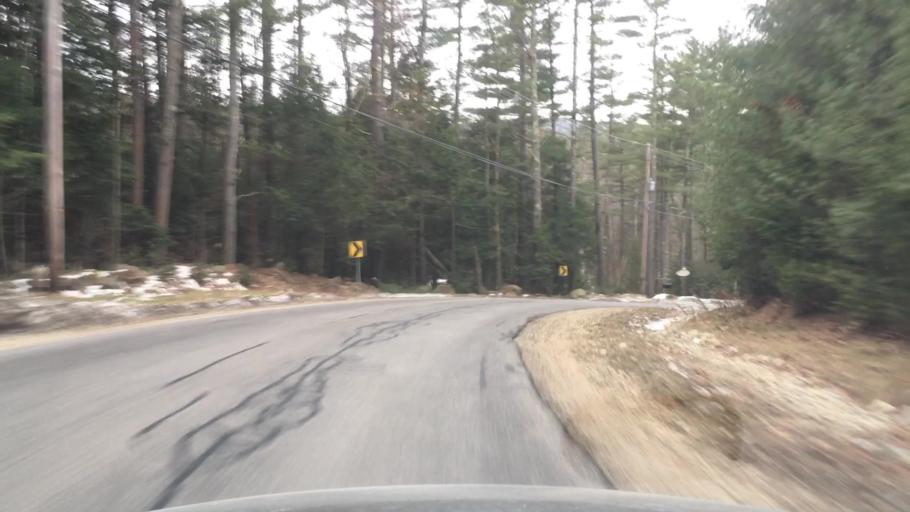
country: US
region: New Hampshire
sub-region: Hillsborough County
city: Goffstown
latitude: 42.9695
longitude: -71.6260
